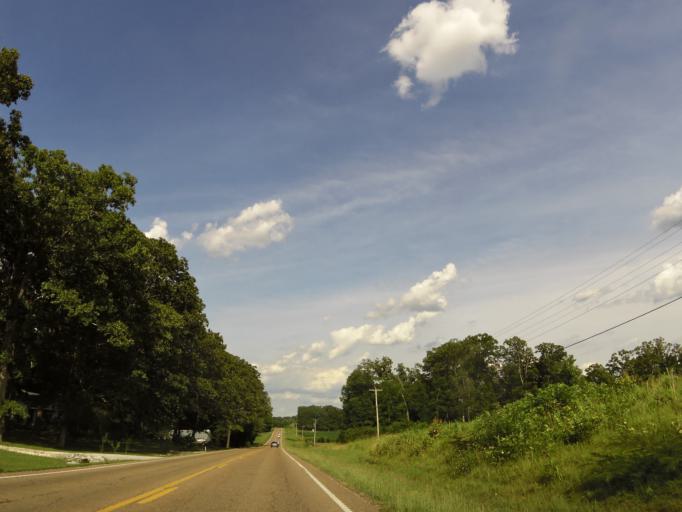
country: US
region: Tennessee
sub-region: Carroll County
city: Huntingdon
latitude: 36.0310
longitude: -88.3485
